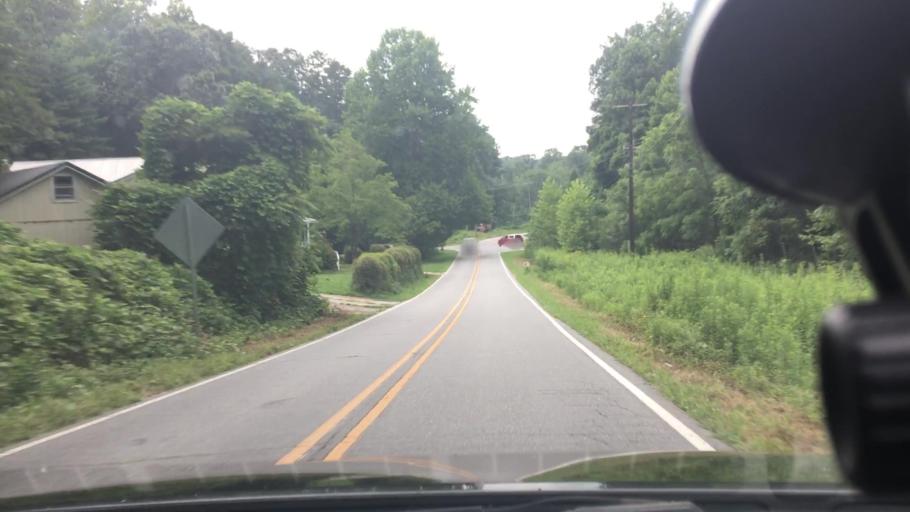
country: US
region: North Carolina
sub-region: McDowell County
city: West Marion
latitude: 35.6554
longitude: -82.0160
